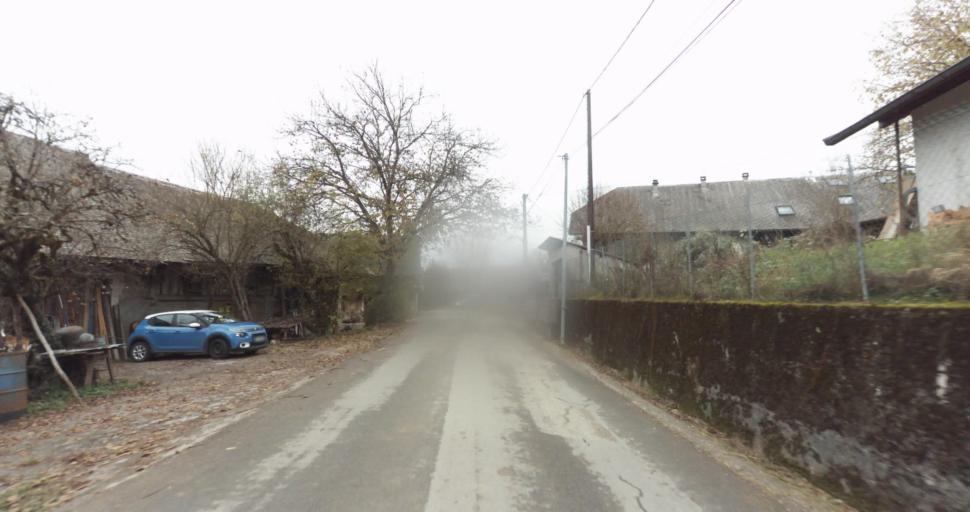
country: FR
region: Rhone-Alpes
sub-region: Departement de la Savoie
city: Albens
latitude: 45.7664
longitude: 5.9658
